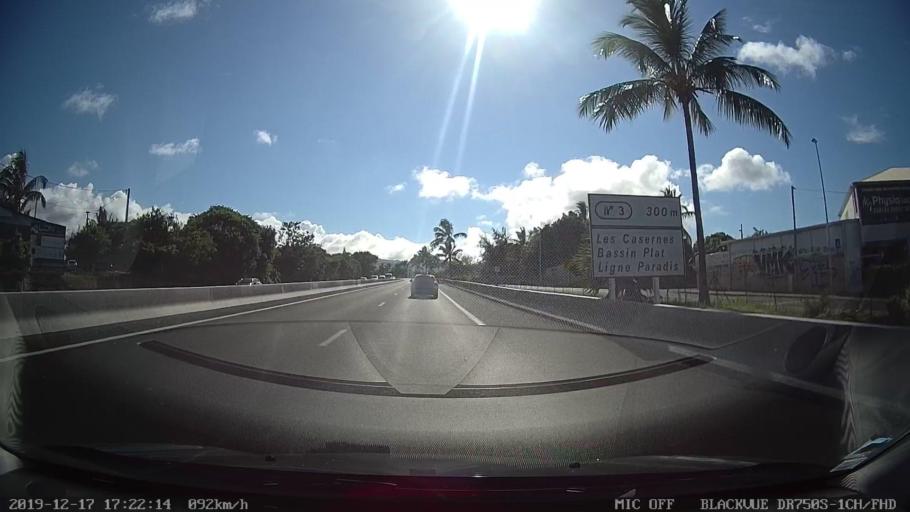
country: RE
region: Reunion
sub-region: Reunion
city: Saint-Pierre
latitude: -21.3228
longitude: 55.4826
